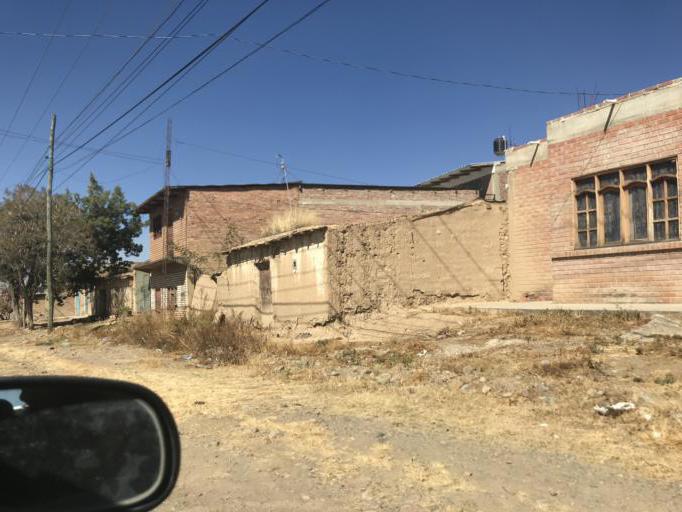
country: BO
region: Cochabamba
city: Tarata
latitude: -17.6025
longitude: -65.9821
